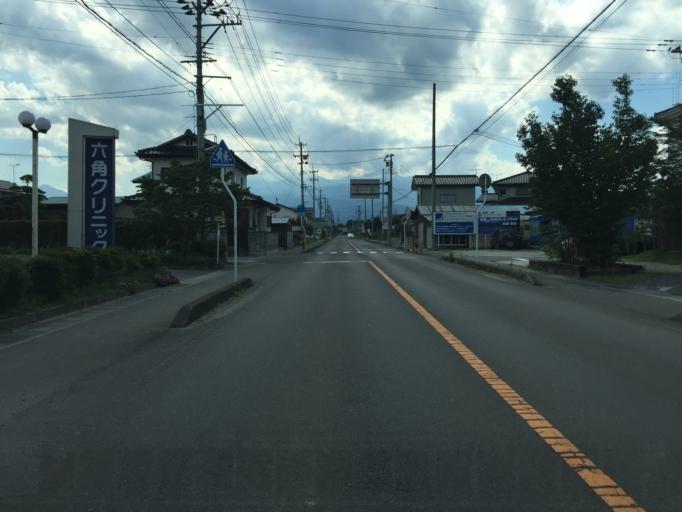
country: JP
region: Fukushima
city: Fukushima-shi
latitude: 37.7492
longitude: 140.4332
